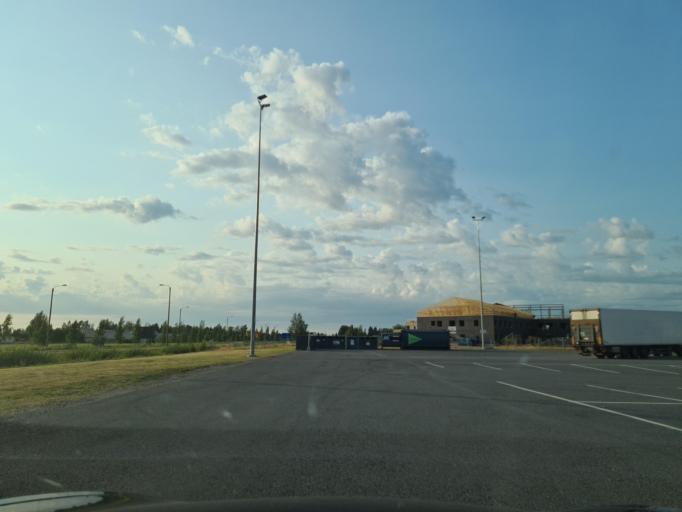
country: FI
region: Southern Ostrobothnia
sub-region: Seinaejoki
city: Kauhava
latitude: 63.0909
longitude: 23.0588
